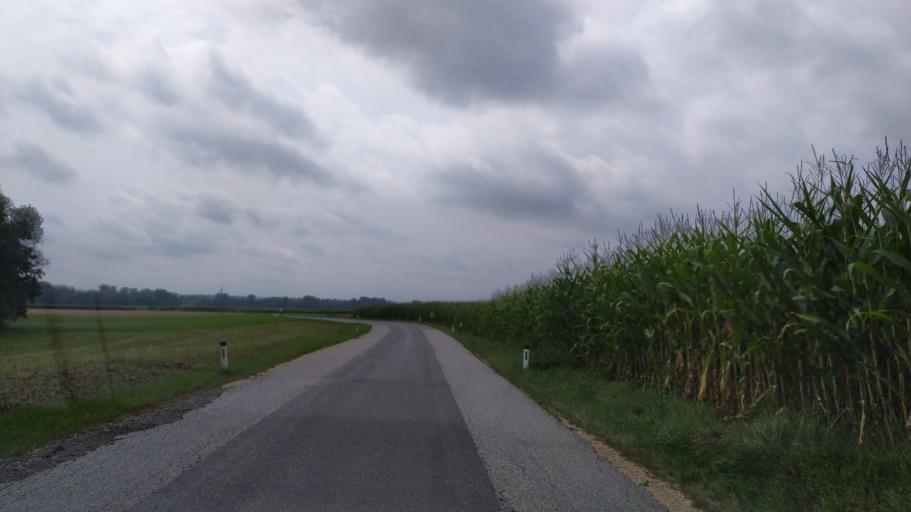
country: AT
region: Upper Austria
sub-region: Politischer Bezirk Perg
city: Bad Kreuzen
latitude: 48.2027
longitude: 14.7847
